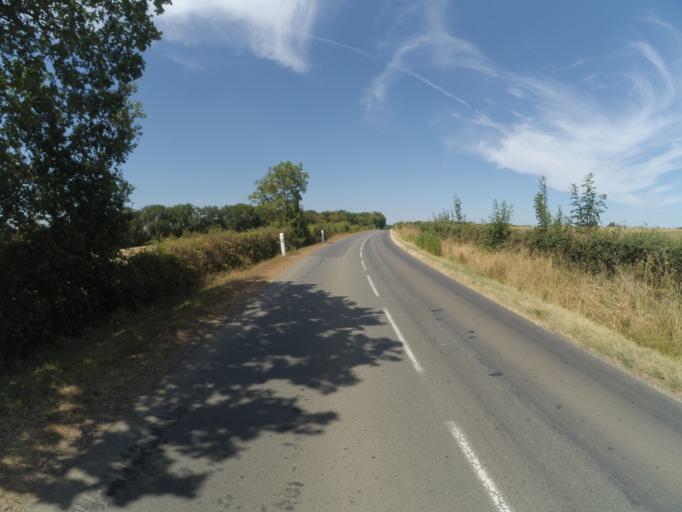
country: FR
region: Poitou-Charentes
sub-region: Departement de la Vienne
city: La Villedieu-du-Clain
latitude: 46.4036
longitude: 0.3426
